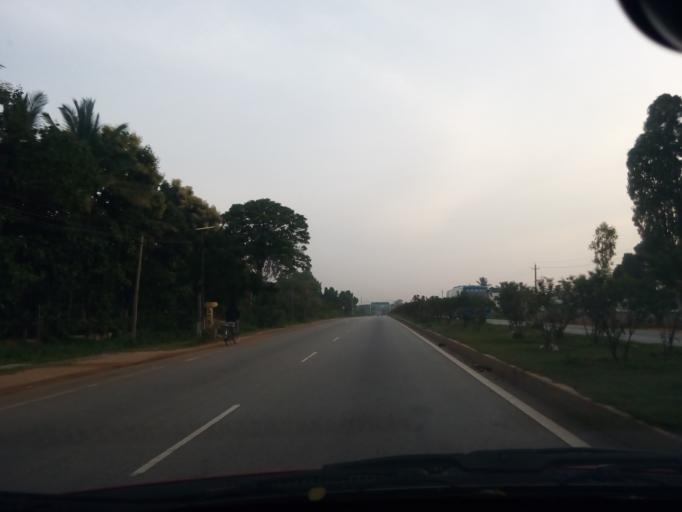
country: IN
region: Karnataka
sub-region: Chikkaballapur
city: Chik Ballapur
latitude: 13.3758
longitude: 77.7260
